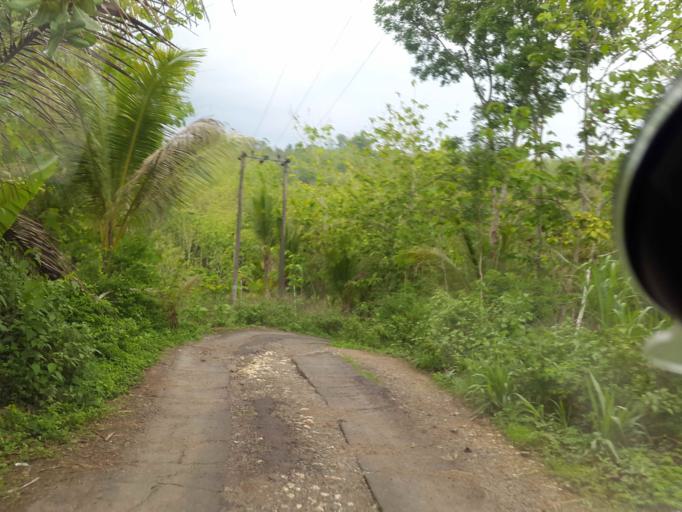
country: ID
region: East Java
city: Tekikbanyuurip
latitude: -8.2141
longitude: 111.9468
